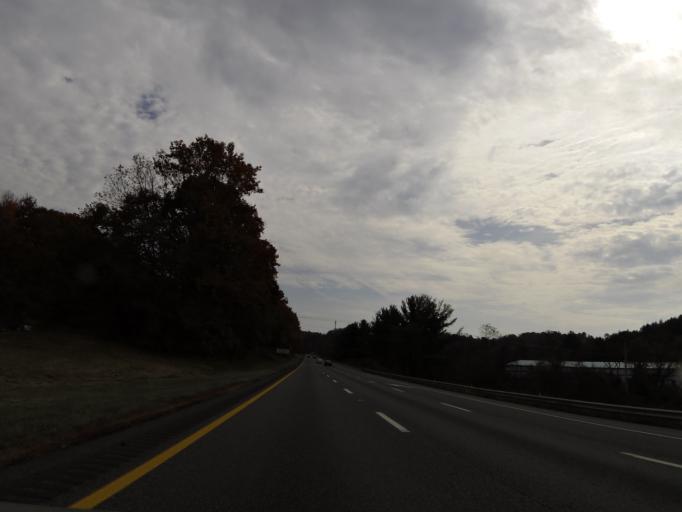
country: US
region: Virginia
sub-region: Carroll County
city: Hillsville
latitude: 36.7424
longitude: -80.7708
